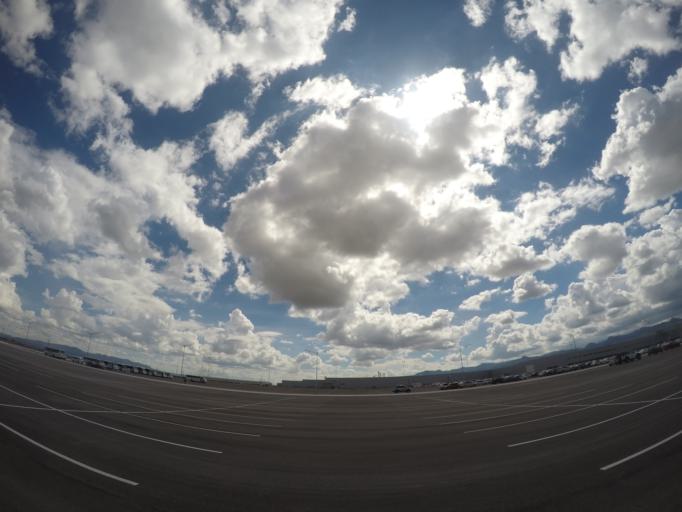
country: MX
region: San Luis Potosi
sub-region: Zaragoza
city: Cerro Gordo
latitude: 21.9670
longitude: -100.8460
